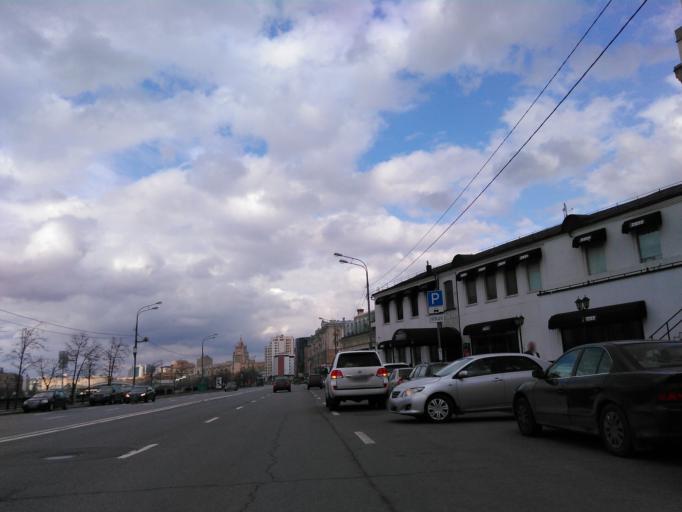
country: RU
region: Moscow
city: Luzhniki
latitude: 55.7325
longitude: 37.5607
